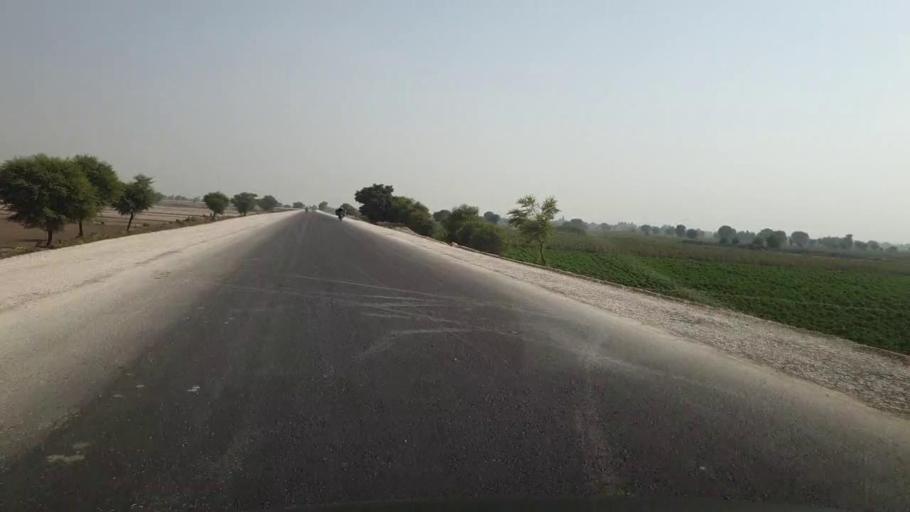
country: PK
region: Sindh
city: Bhan
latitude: 26.5573
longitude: 67.7764
